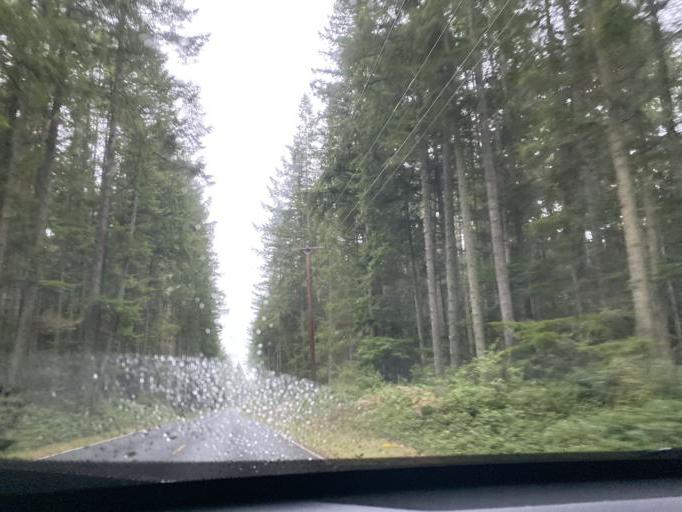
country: US
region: Washington
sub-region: Island County
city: Langley
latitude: 48.0321
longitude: -122.4629
